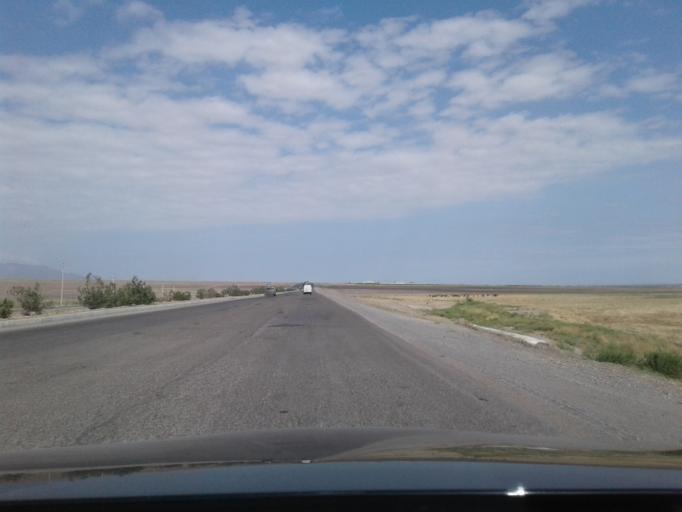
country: TM
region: Ahal
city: Baharly
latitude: 38.4553
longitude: 57.3654
